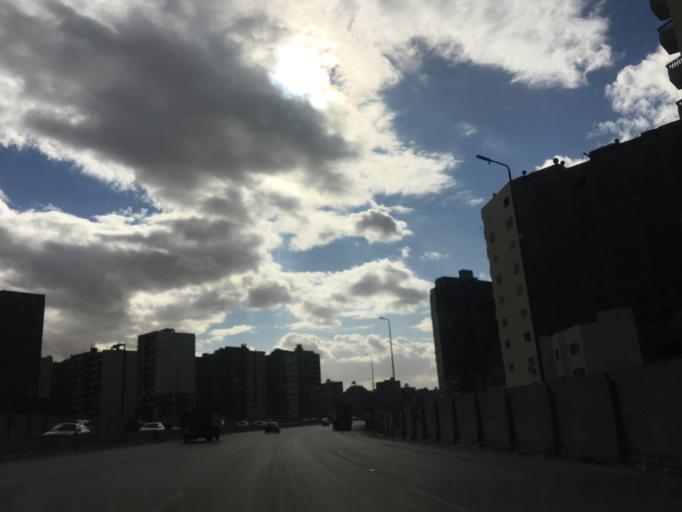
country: EG
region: Al Jizah
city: Al Jizah
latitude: 30.0167
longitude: 31.1656
